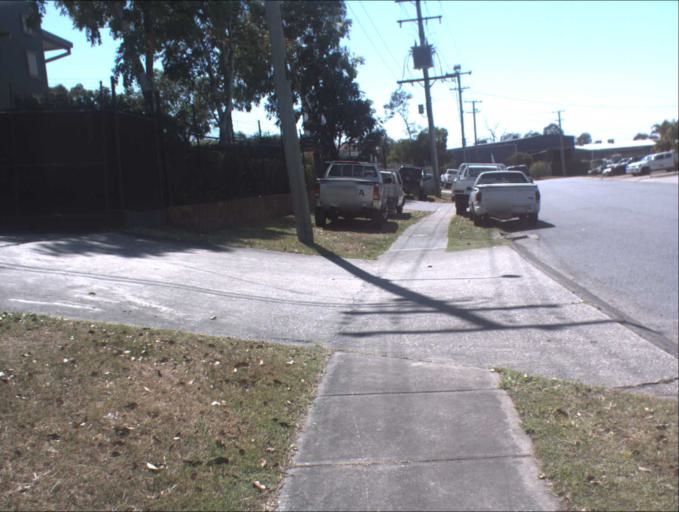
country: AU
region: Queensland
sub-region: Logan
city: Logan City
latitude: -27.6651
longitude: 153.1153
